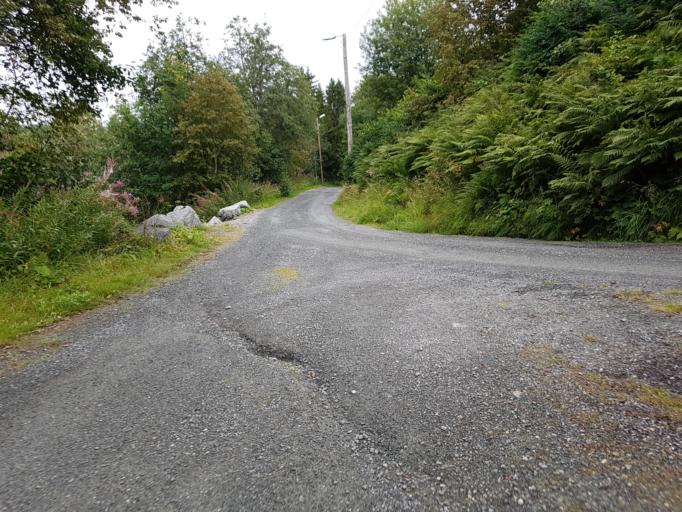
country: NO
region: Sor-Trondelag
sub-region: Trondheim
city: Trondheim
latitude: 63.3834
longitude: 10.3509
